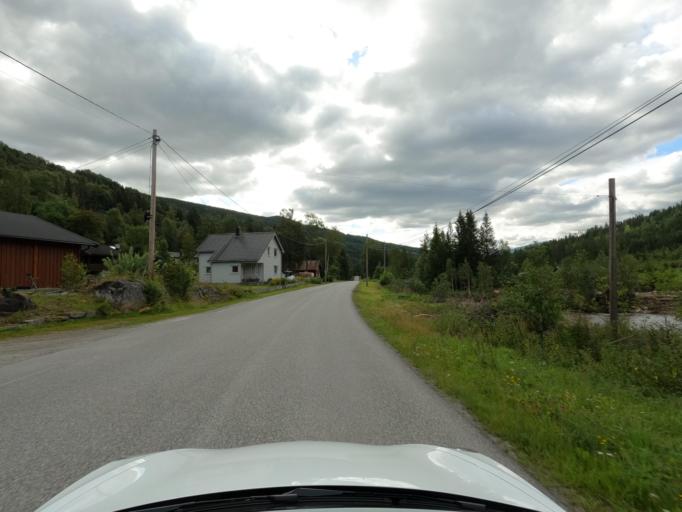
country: NO
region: Buskerud
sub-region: Nore og Uvdal
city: Rodberg
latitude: 60.0280
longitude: 8.8286
